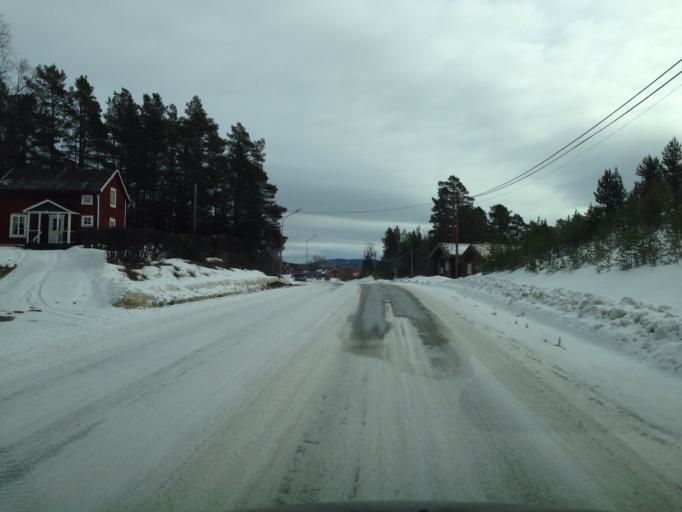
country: SE
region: Jaemtland
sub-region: Harjedalens Kommun
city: Sveg
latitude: 62.1131
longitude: 13.2631
